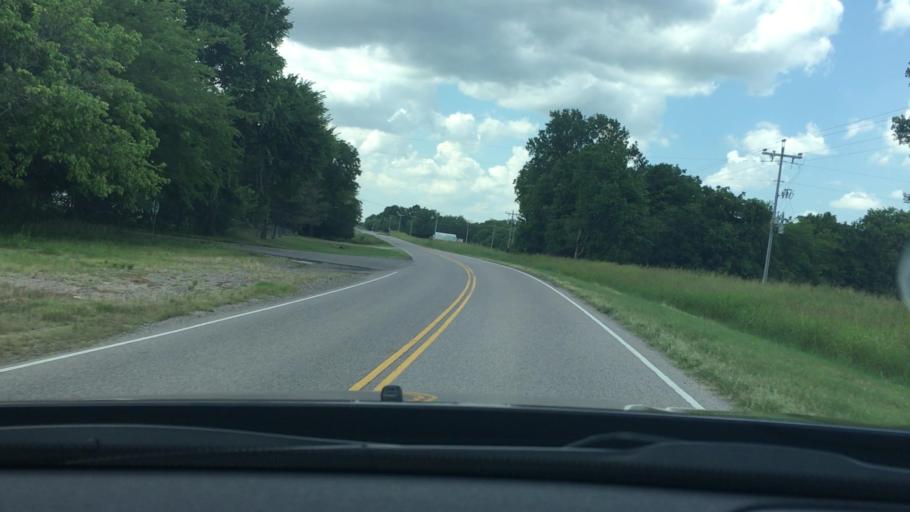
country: US
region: Oklahoma
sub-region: Johnston County
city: Tishomingo
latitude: 34.4844
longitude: -96.6266
